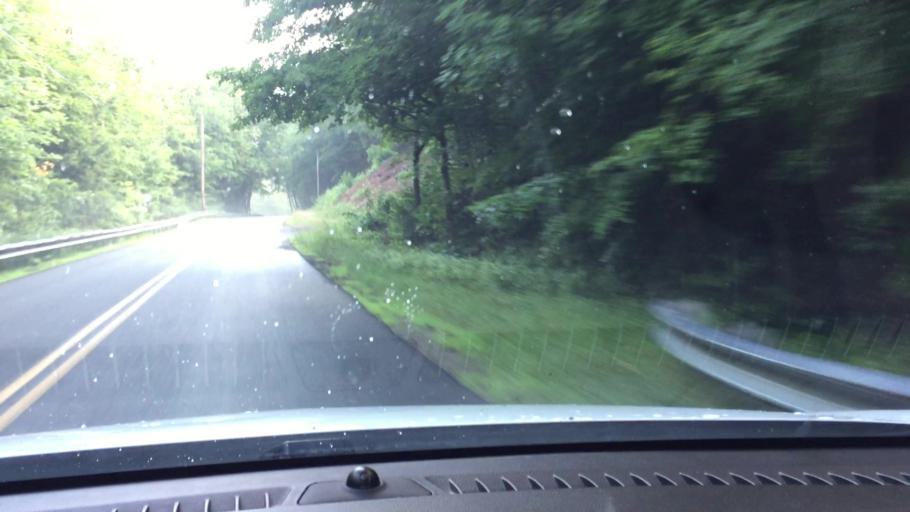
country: US
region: Massachusetts
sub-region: Berkshire County
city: Becket
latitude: 42.3982
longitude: -72.9802
